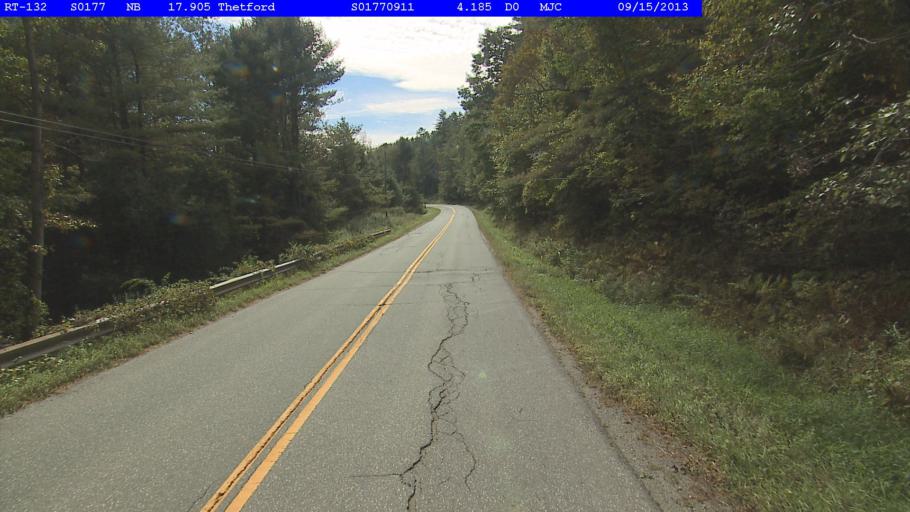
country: US
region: New Hampshire
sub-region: Grafton County
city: Hanover
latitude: 43.7996
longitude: -72.2655
